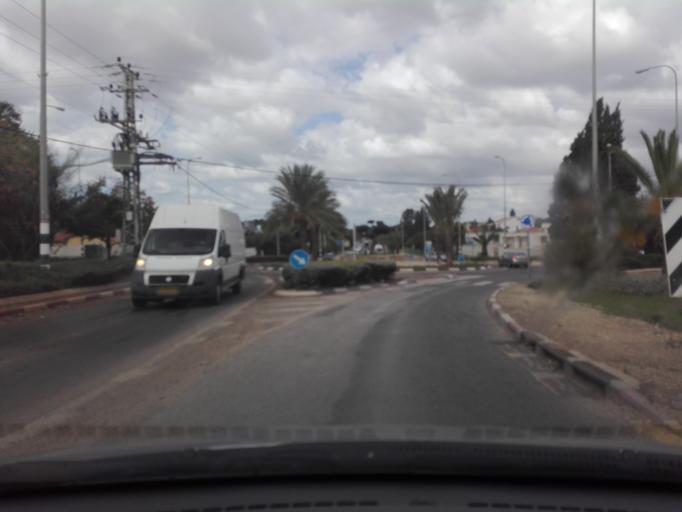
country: IL
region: Haifa
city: Hadera
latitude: 32.4719
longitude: 34.9788
